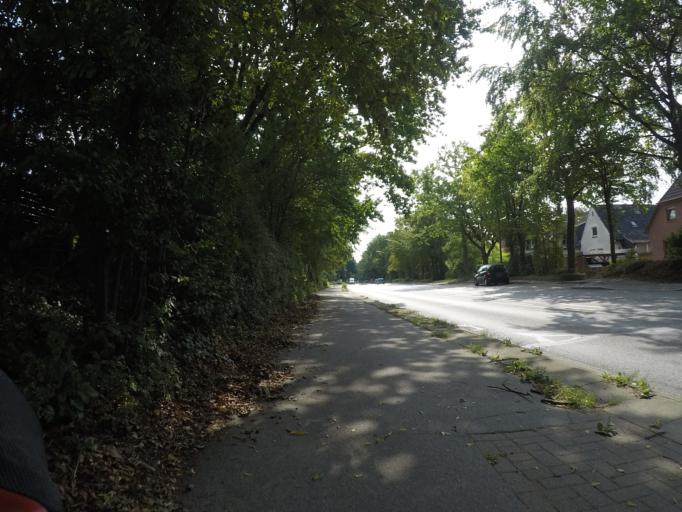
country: DE
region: Hamburg
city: Poppenbuettel
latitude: 53.6699
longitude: 10.0639
